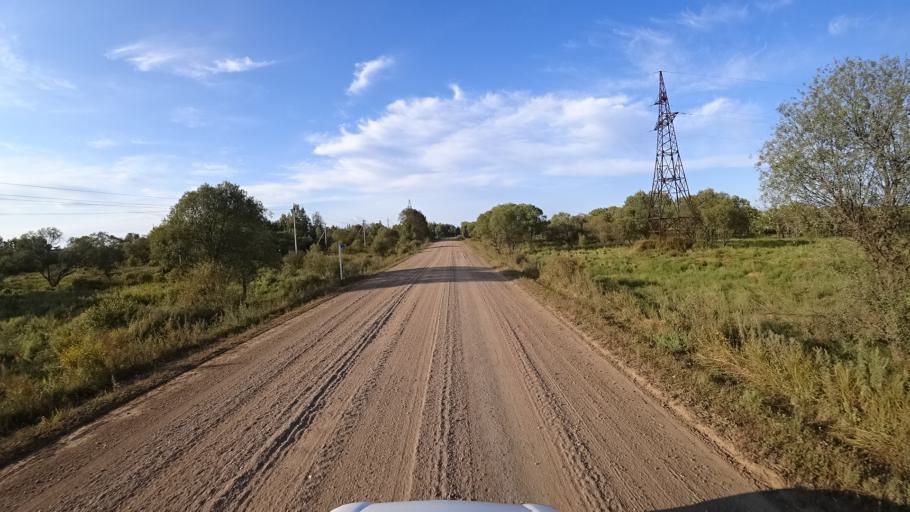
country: RU
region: Amur
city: Arkhara
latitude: 49.3651
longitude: 130.1363
